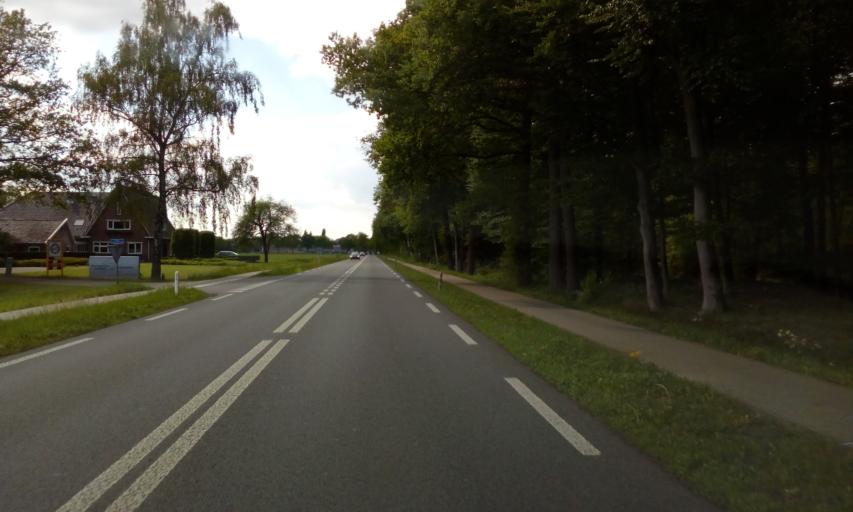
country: NL
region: Gelderland
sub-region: Gemeente Voorst
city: Voorst
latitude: 52.1869
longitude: 6.1039
